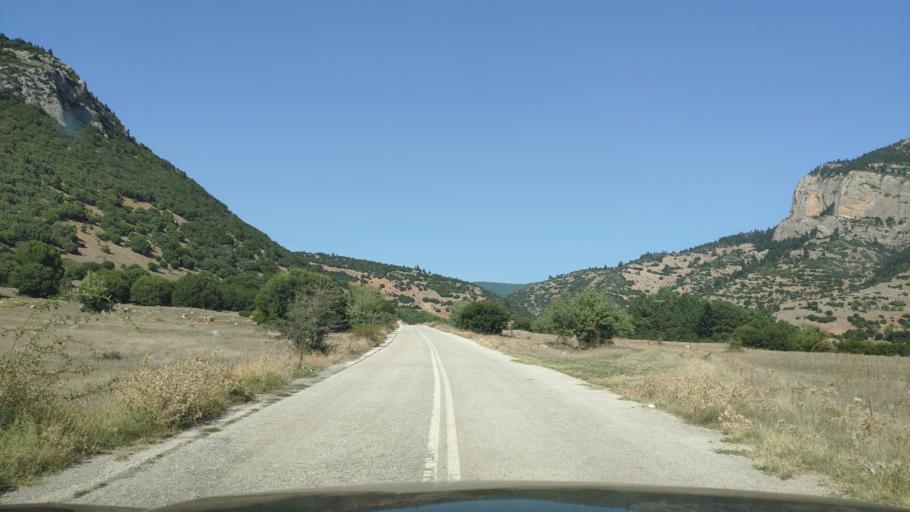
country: GR
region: West Greece
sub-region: Nomos Achaias
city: Aiyira
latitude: 37.9630
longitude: 22.3458
